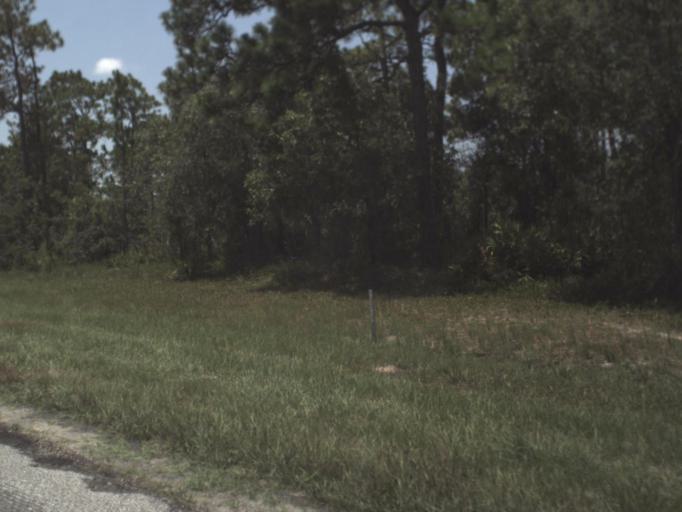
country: US
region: Florida
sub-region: Citrus County
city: Sugarmill Woods
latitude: 28.6485
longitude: -82.5523
